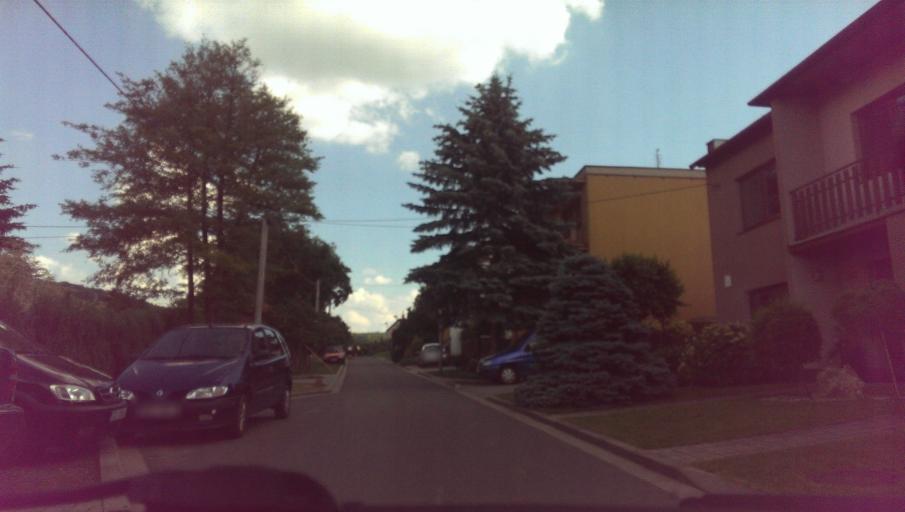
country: CZ
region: Zlin
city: Popovice
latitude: 49.0353
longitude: 17.5052
